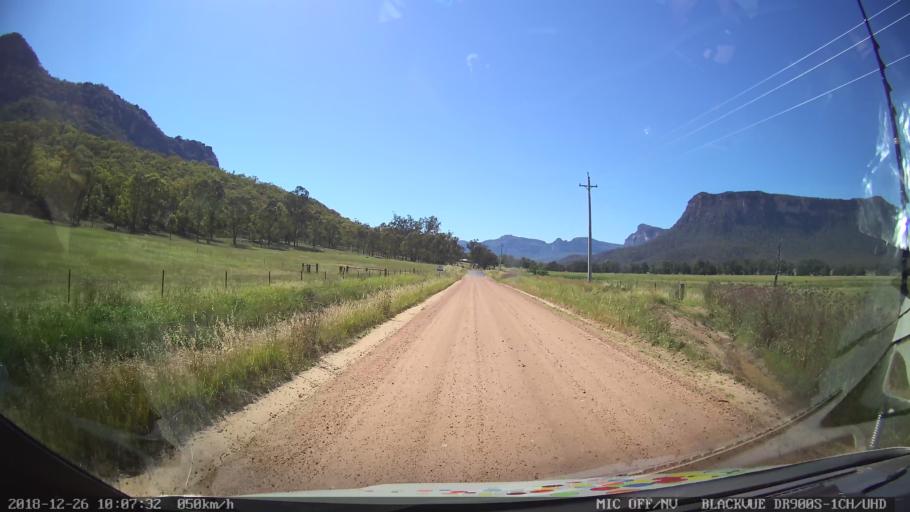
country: AU
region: New South Wales
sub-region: Mid-Western Regional
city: Kandos
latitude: -33.0913
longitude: 150.2249
